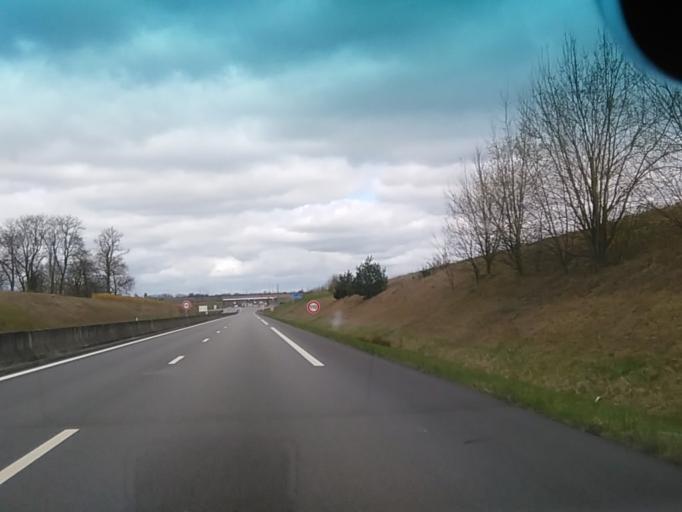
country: FR
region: Haute-Normandie
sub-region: Departement de l'Eure
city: Bourg-Achard
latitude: 49.3488
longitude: 0.8354
